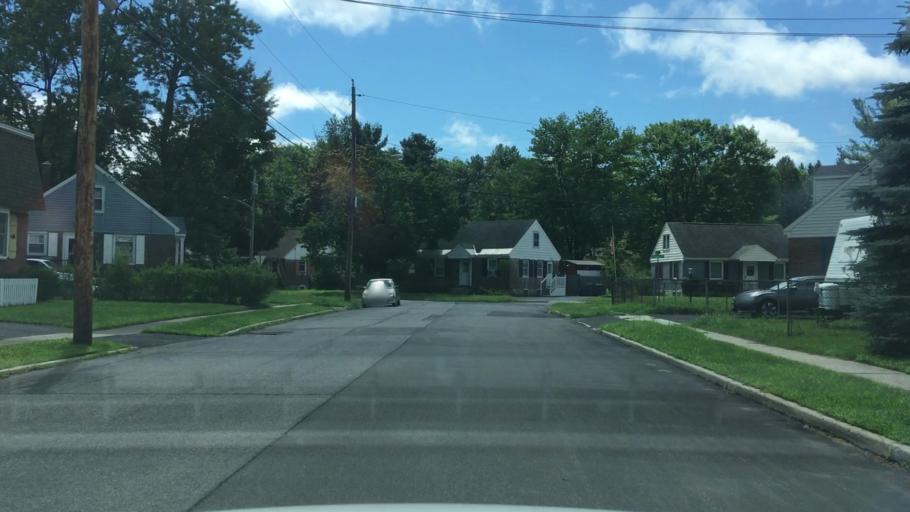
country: US
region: New York
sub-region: Albany County
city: Colonie
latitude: 42.7419
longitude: -73.8548
